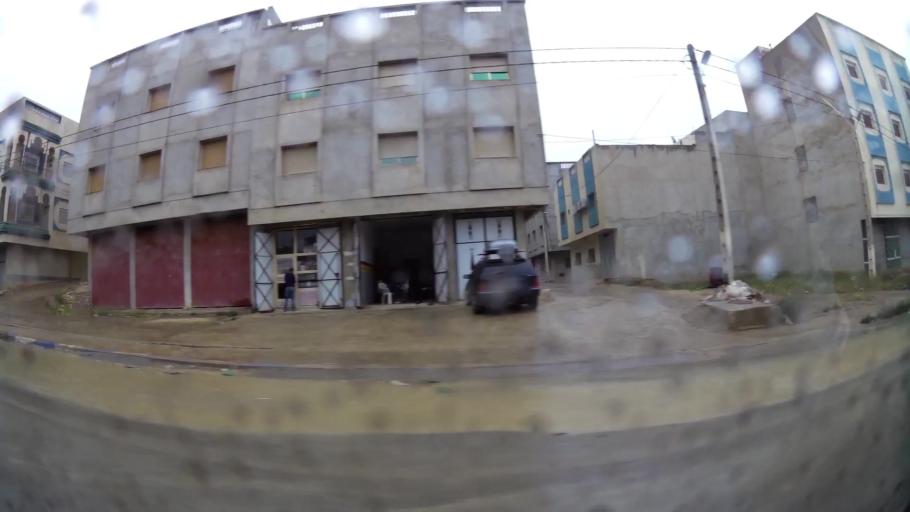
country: MA
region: Oriental
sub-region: Nador
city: Midar
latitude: 34.8837
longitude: -3.7268
